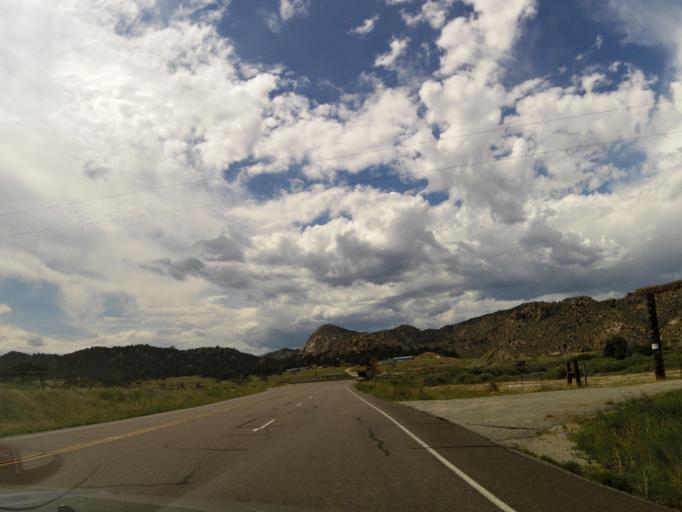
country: US
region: Colorado
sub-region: Custer County
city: Westcliffe
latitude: 38.3928
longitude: -105.6245
